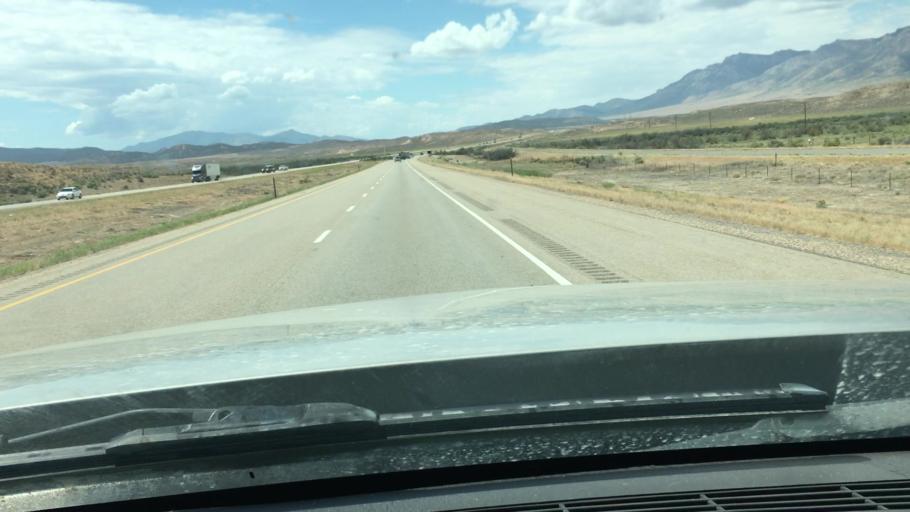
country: US
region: Utah
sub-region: Sanpete County
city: Gunnison
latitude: 39.4145
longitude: -112.0492
